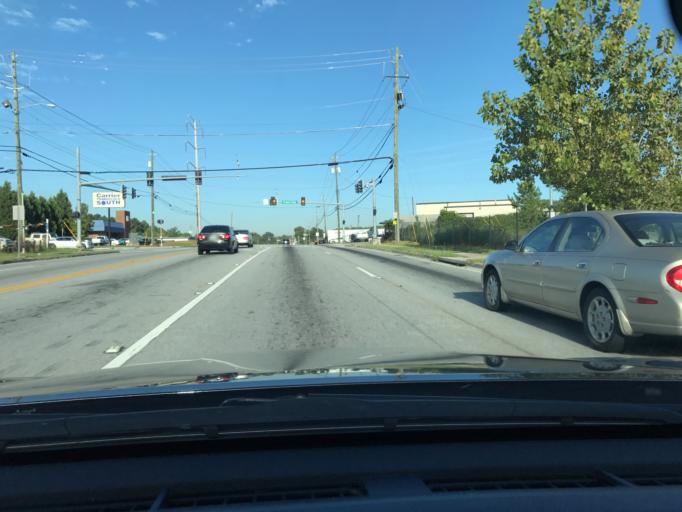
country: US
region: Georgia
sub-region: Clayton County
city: Lake City
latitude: 33.6105
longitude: -84.3299
